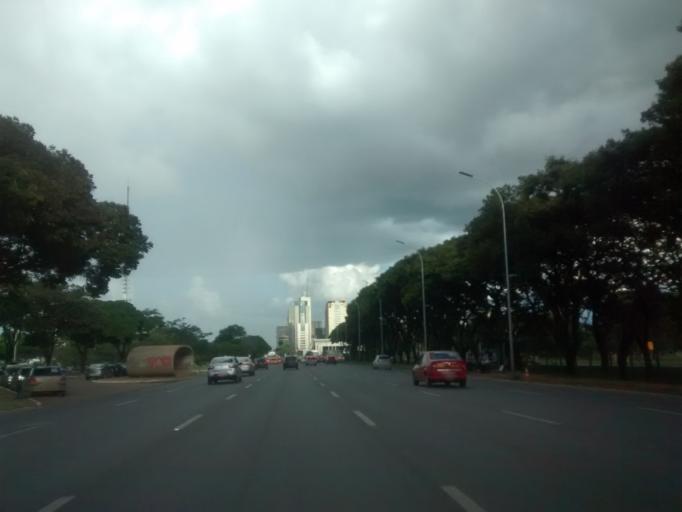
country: BR
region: Federal District
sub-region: Brasilia
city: Brasilia
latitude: -15.7901
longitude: -47.9008
